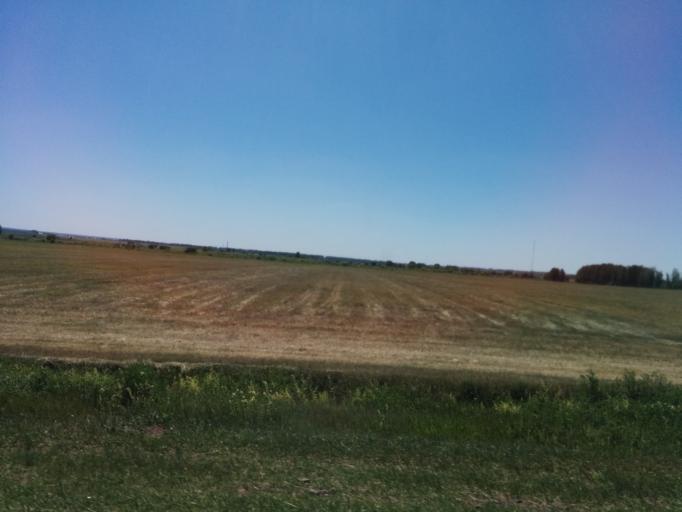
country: RU
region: Tambov
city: Donskoye
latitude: 52.8375
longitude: 41.4357
